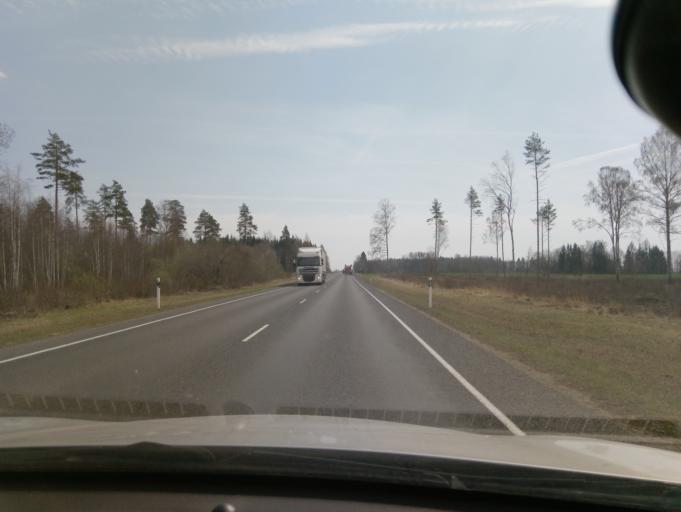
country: EE
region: Viljandimaa
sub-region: Vohma linn
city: Vohma
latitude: 58.7195
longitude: 25.6071
